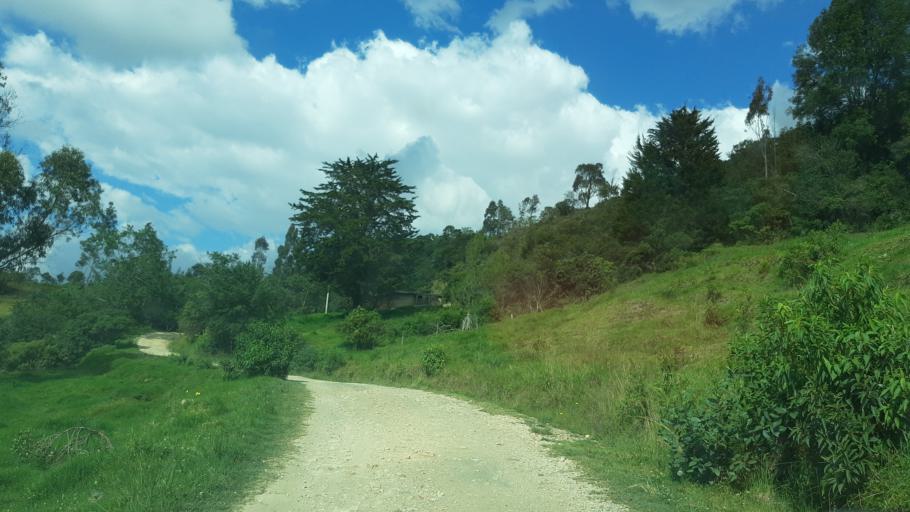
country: CO
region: Boyaca
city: Santa Sofia
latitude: 5.7342
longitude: -73.5524
